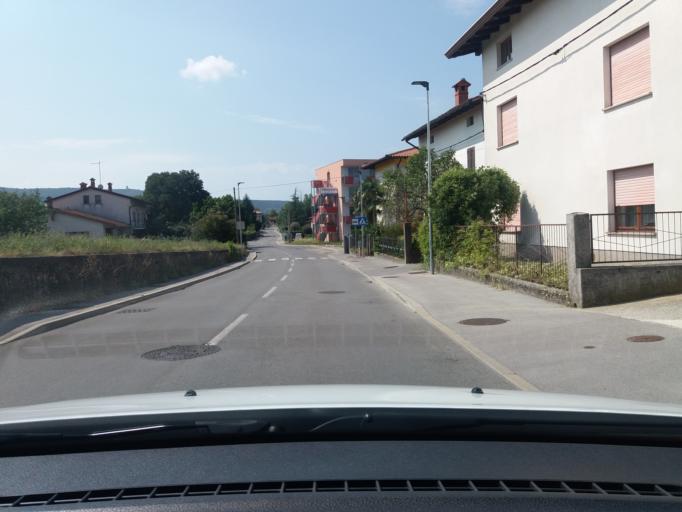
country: SI
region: Sempeter-Vrtojba
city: Vrtojba
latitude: 45.9073
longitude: 13.6299
